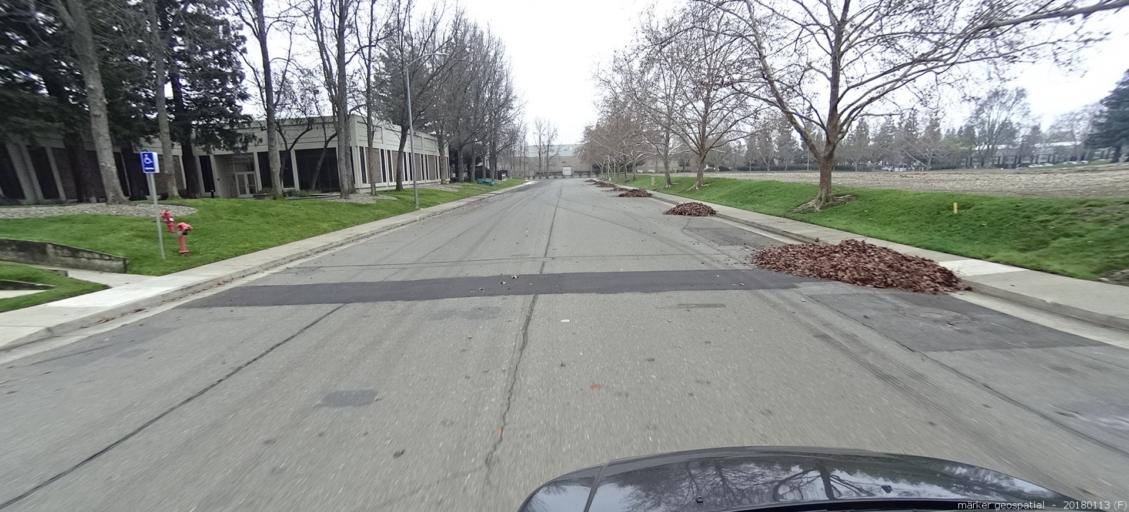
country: US
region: California
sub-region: Sacramento County
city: Rancho Cordova
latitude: 38.5930
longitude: -121.2728
